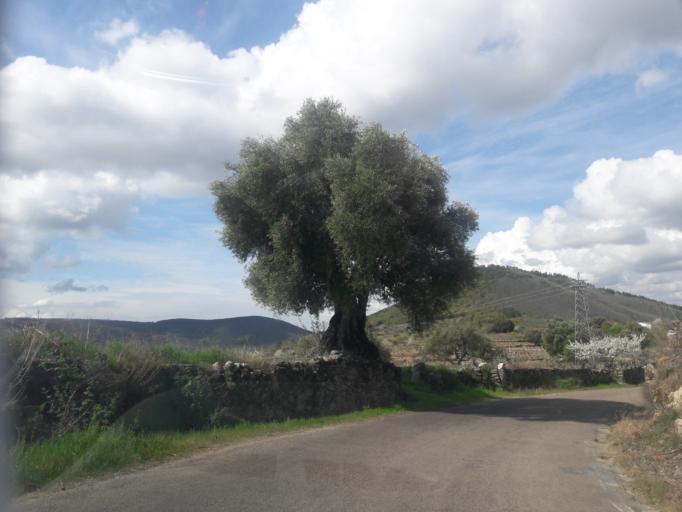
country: ES
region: Castille and Leon
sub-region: Provincia de Salamanca
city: San Esteban de la Sierra
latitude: 40.5049
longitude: -5.8975
